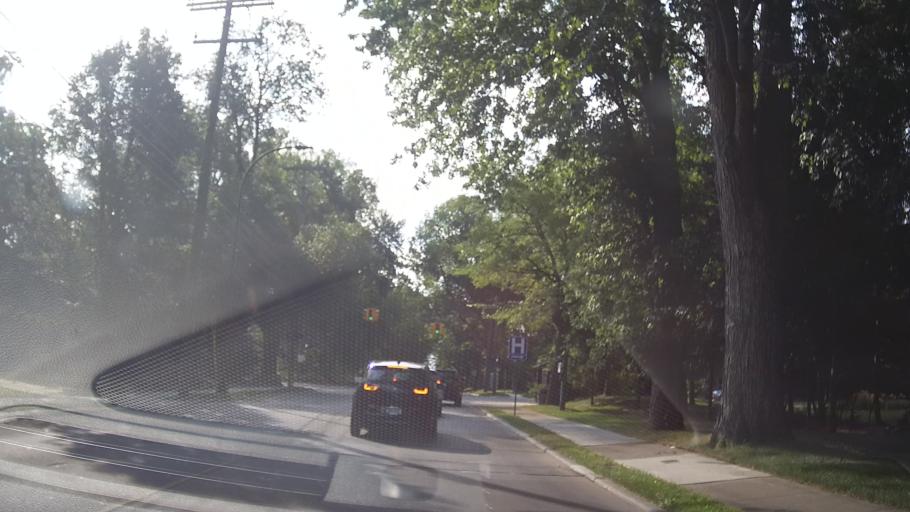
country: US
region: Michigan
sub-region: Wayne County
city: Grosse Pointe Farms
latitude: 42.4097
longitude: -82.8927
